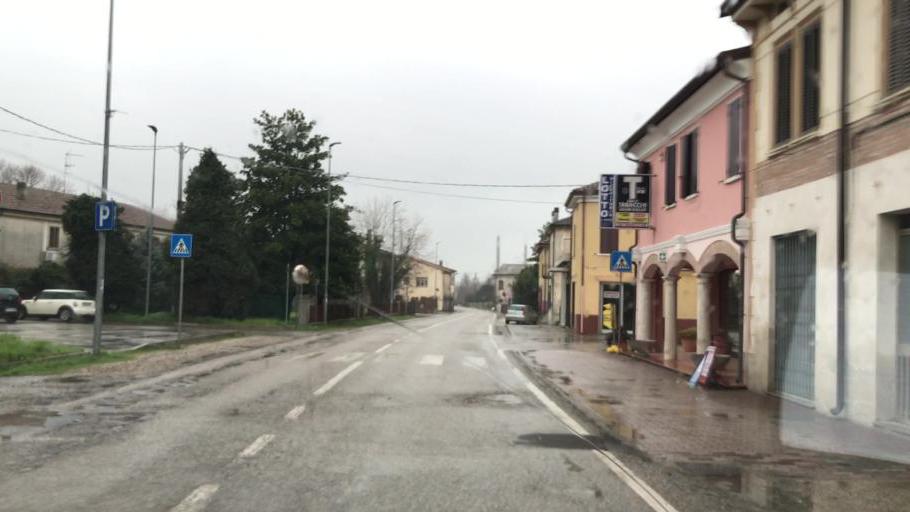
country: IT
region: Veneto
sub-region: Provincia di Rovigo
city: Castelnovo Bariano
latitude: 45.0140
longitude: 11.2663
